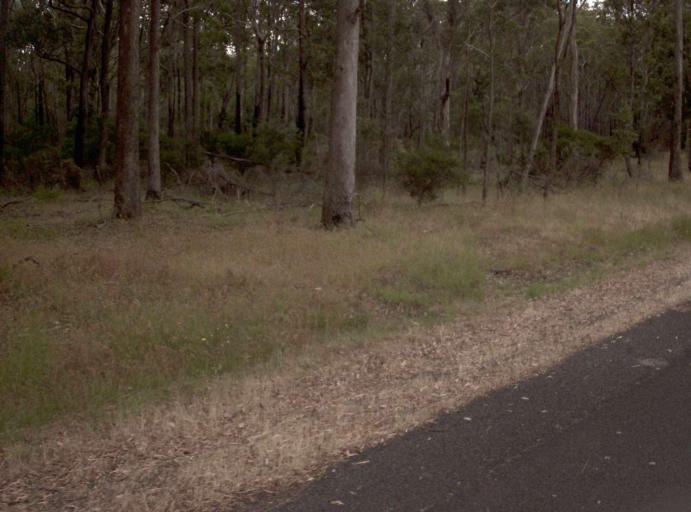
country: AU
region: Victoria
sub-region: Wellington
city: Sale
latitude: -38.4460
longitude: 146.9433
